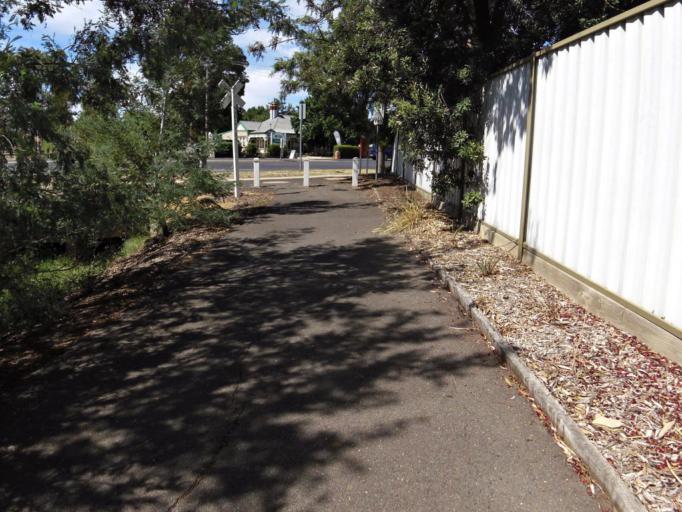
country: AU
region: Victoria
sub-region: Greater Bendigo
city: White Hills
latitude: -36.7418
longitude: 144.2965
